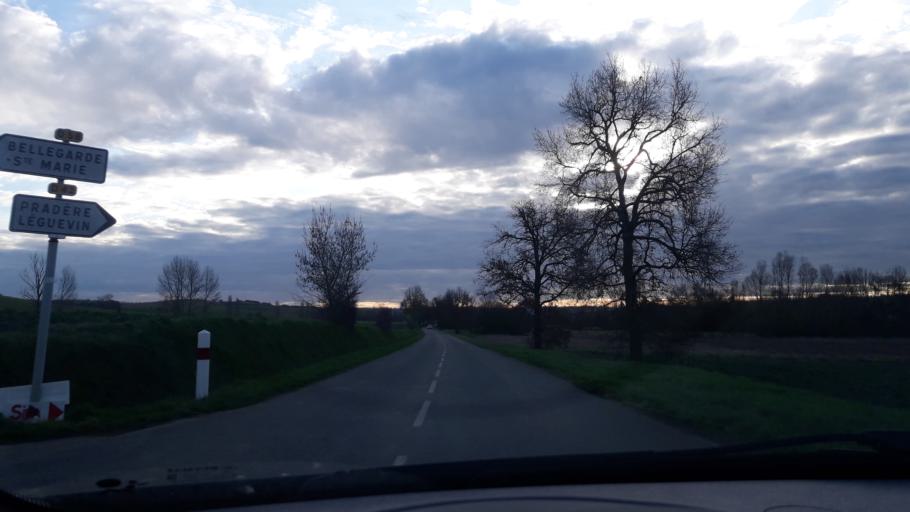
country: FR
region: Midi-Pyrenees
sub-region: Departement du Gers
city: Pujaudran
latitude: 43.6588
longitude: 1.1097
